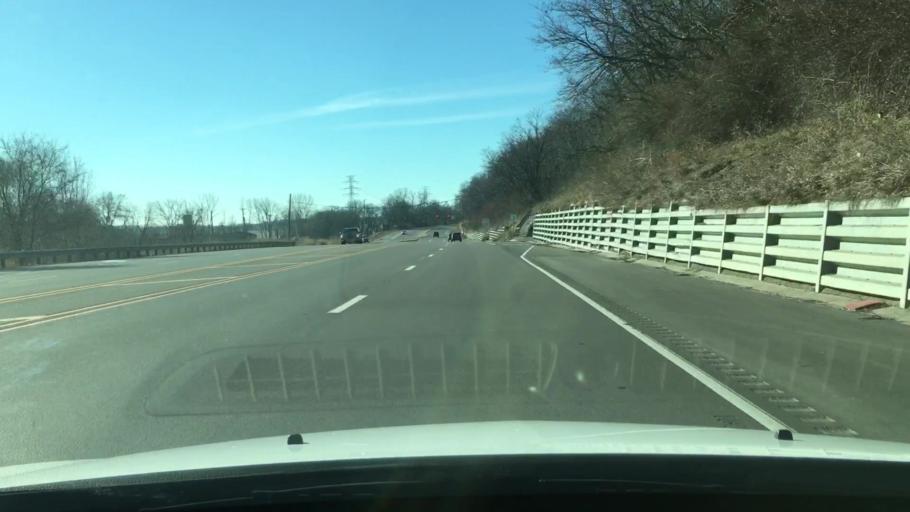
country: US
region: Illinois
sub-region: Tazewell County
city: Pekin
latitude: 40.5914
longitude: -89.6762
